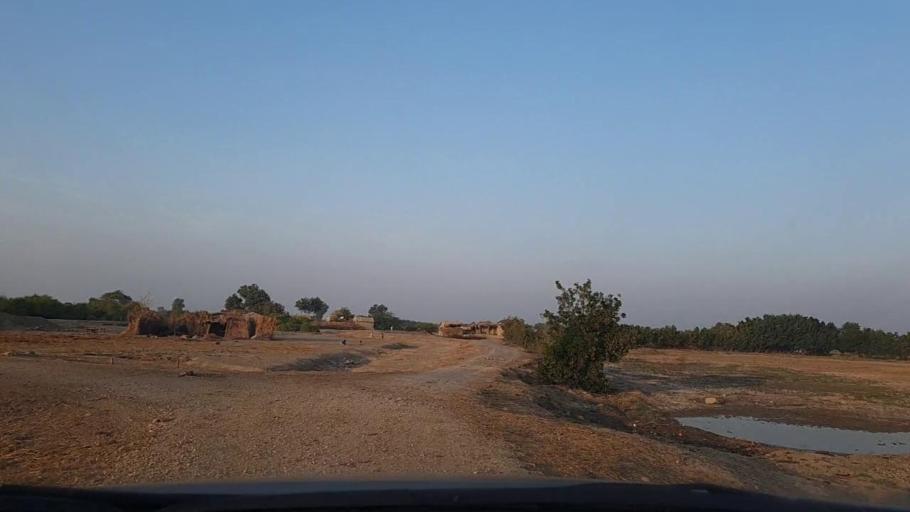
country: PK
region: Sindh
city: Mirpur Sakro
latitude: 24.5628
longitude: 67.6614
